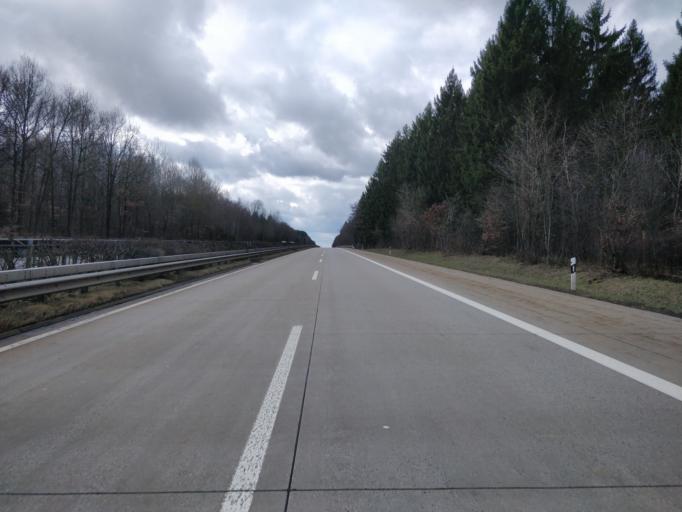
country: DE
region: Rheinland-Pfalz
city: Brockscheid
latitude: 50.1306
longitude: 6.8584
